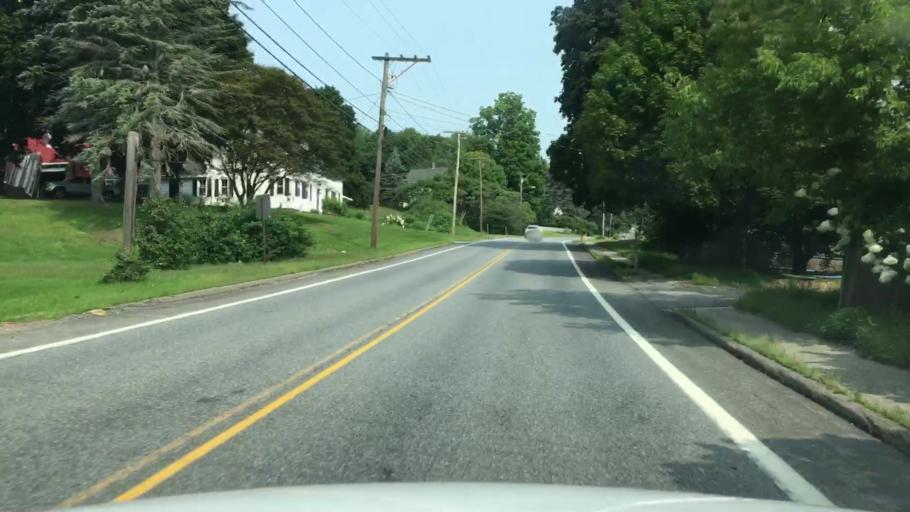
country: US
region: Maine
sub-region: Kennebec County
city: Winthrop
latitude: 44.3124
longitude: -69.9776
